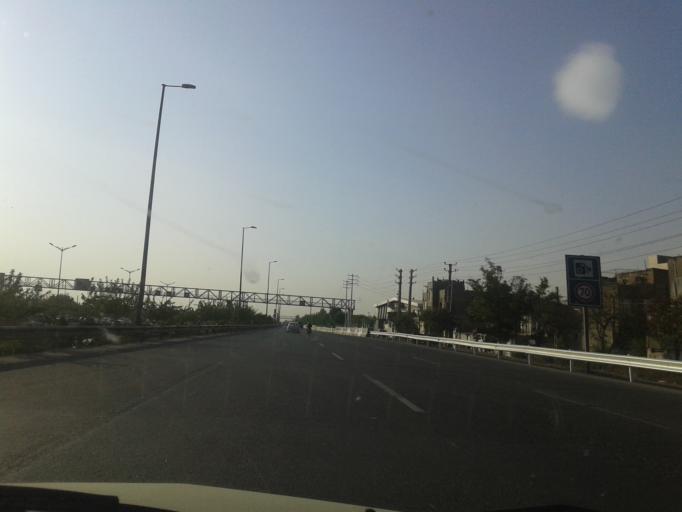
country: IR
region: Tehran
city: Eslamshahr
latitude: 35.6530
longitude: 51.2676
